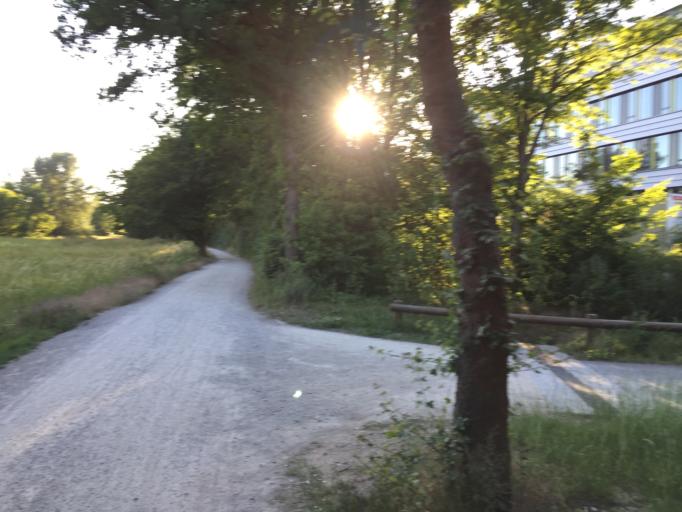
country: DE
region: Bavaria
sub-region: Regierungsbezirk Mittelfranken
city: Erlangen
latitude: 49.5699
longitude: 11.0090
